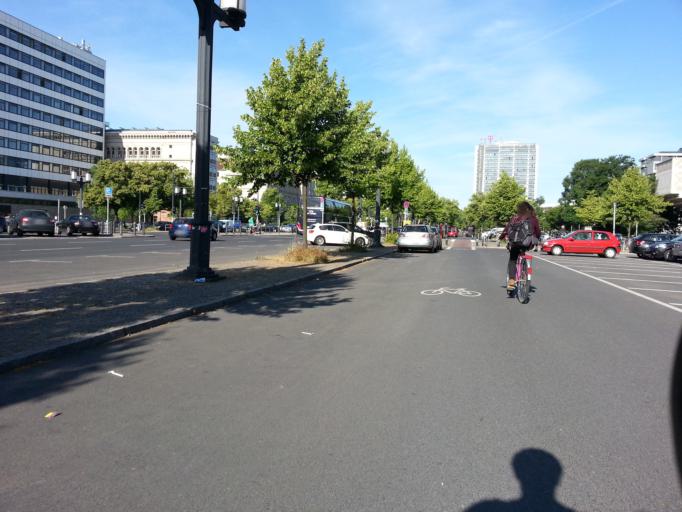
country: DE
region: Berlin
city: Hansaviertel
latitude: 52.5132
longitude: 13.3277
